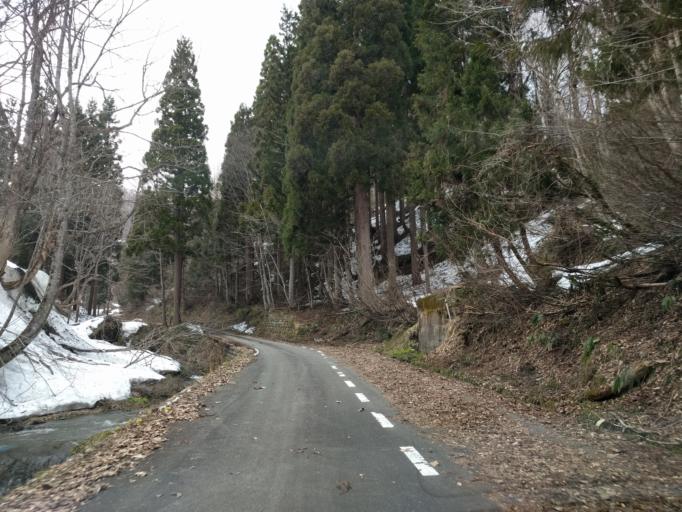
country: JP
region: Niigata
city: Muramatsu
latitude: 37.3398
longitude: 139.4674
